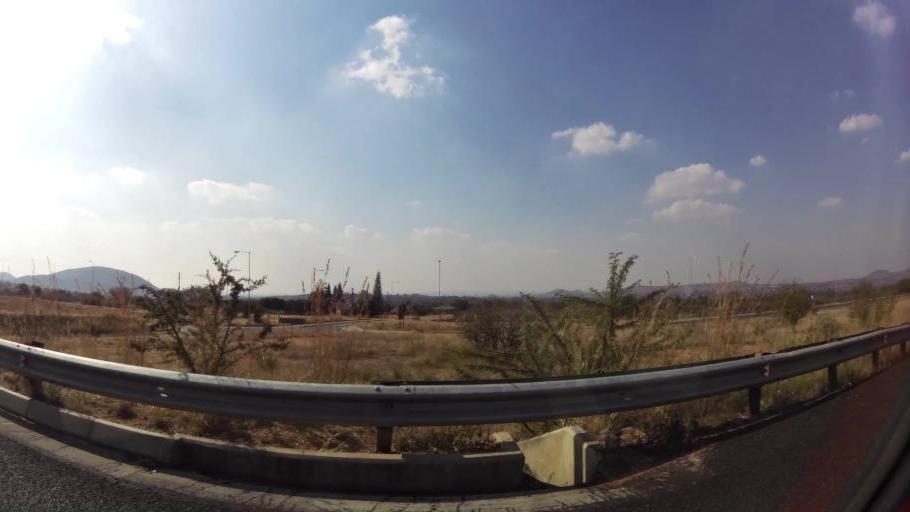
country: ZA
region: North-West
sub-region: Bojanala Platinum District Municipality
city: Rustenburg
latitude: -25.6006
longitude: 27.1333
